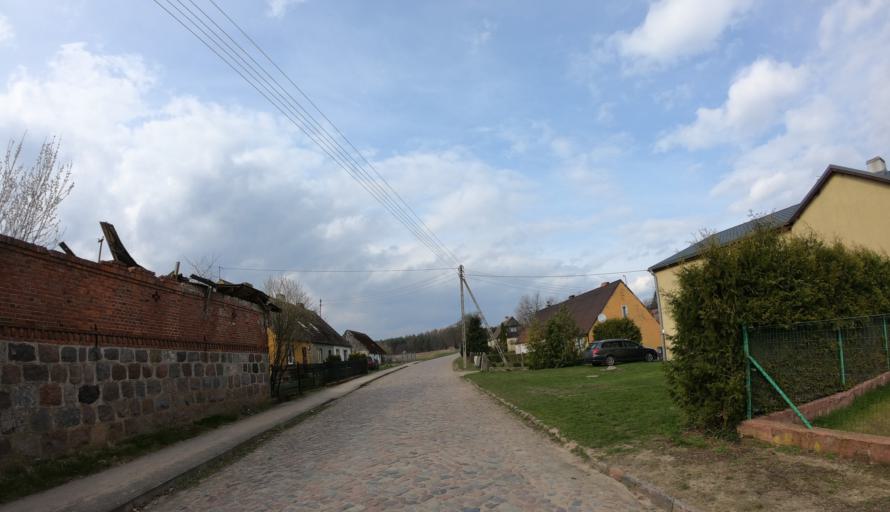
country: PL
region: West Pomeranian Voivodeship
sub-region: Powiat swidwinski
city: Swidwin
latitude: 53.8413
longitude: 15.8452
